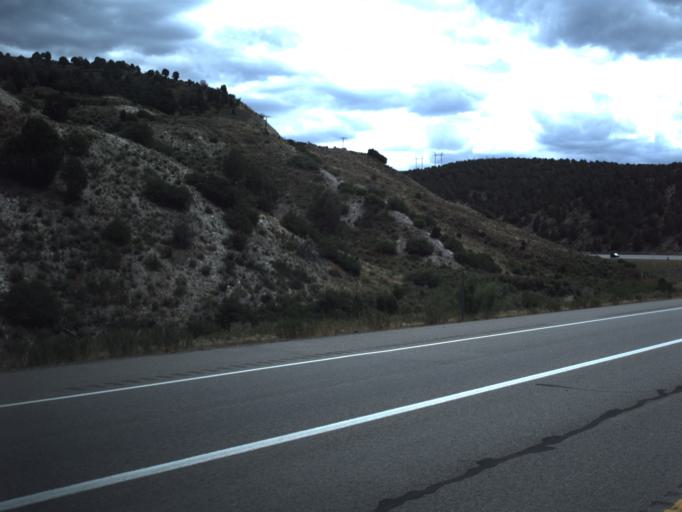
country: US
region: Utah
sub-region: Sanpete County
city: Fairview
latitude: 39.9351
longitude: -111.1996
